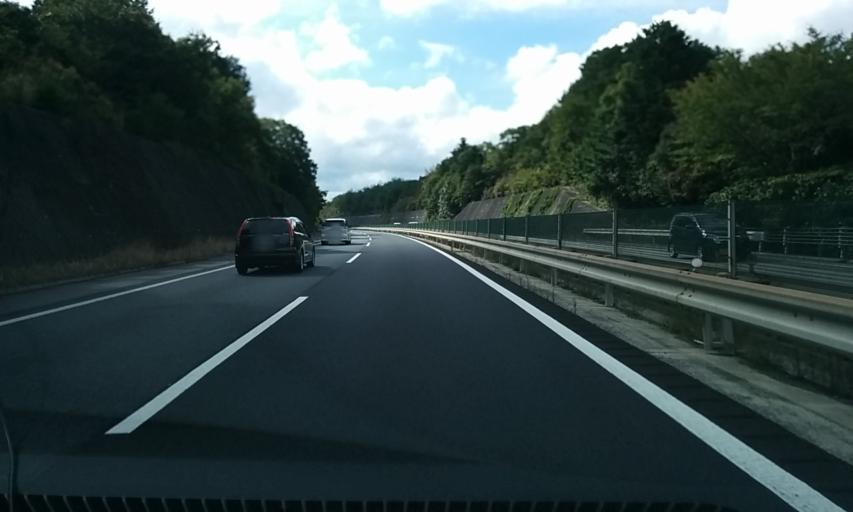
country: JP
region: Hyogo
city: Sandacho
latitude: 34.9161
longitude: 135.1543
